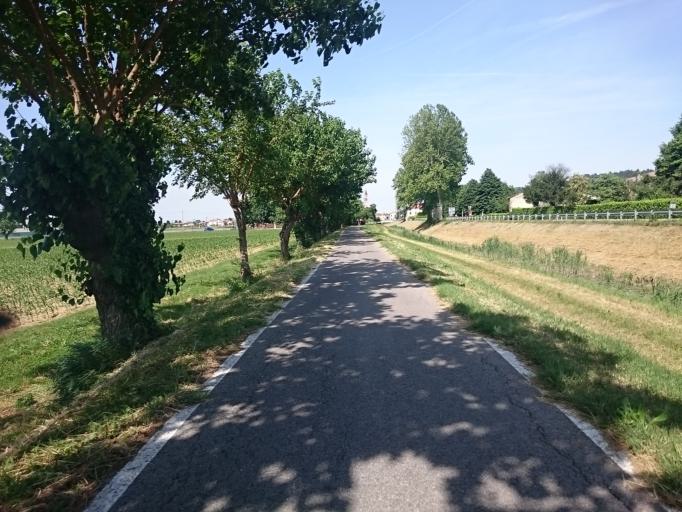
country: IT
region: Veneto
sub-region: Provincia di Padova
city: Bastia
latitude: 45.3797
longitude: 11.6456
